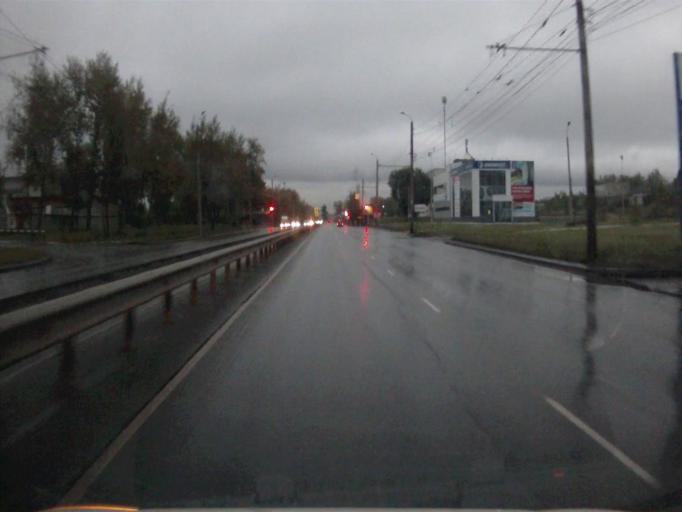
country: RU
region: Chelyabinsk
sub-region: Gorod Chelyabinsk
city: Chelyabinsk
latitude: 55.1375
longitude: 61.4600
